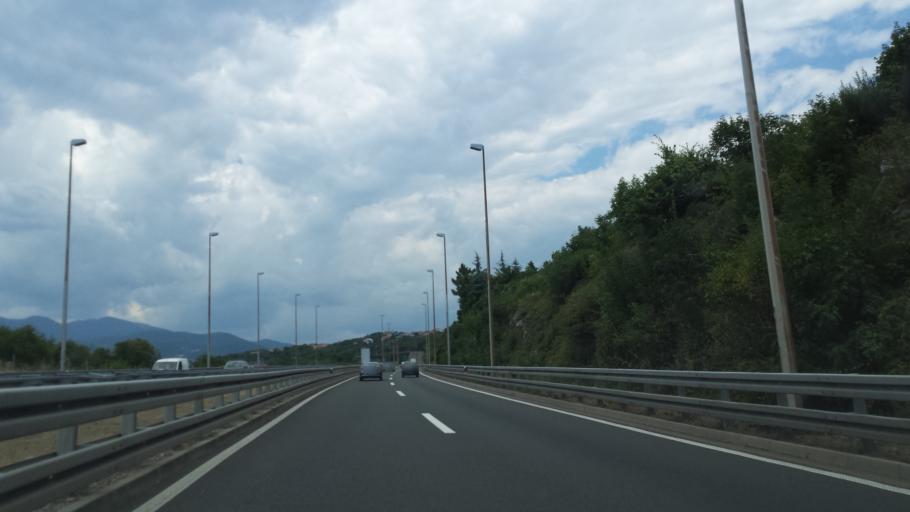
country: HR
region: Primorsko-Goranska
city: Rubesi
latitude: 45.3501
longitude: 14.3620
